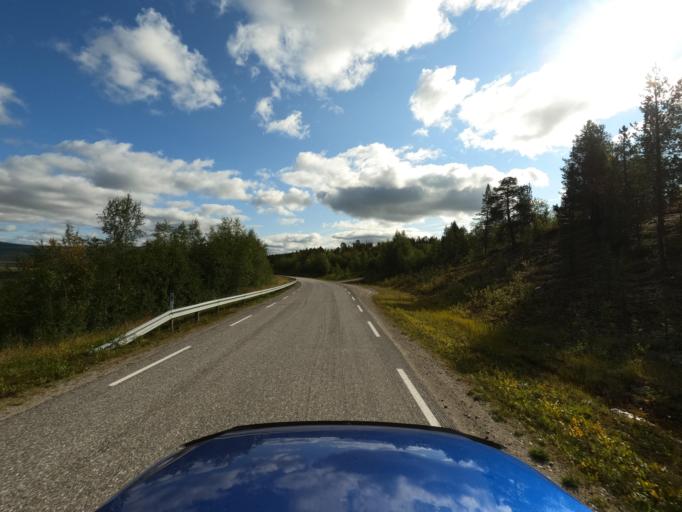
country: NO
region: Finnmark Fylke
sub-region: Karasjok
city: Karasjohka
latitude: 69.4337
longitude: 25.7148
